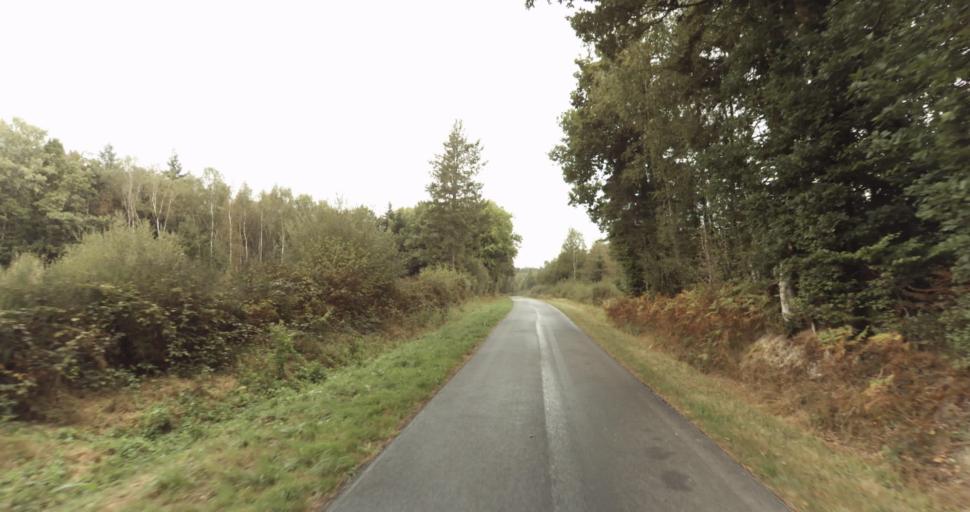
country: FR
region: Lower Normandy
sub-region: Departement de l'Orne
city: Gace
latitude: 48.8169
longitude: 0.3402
